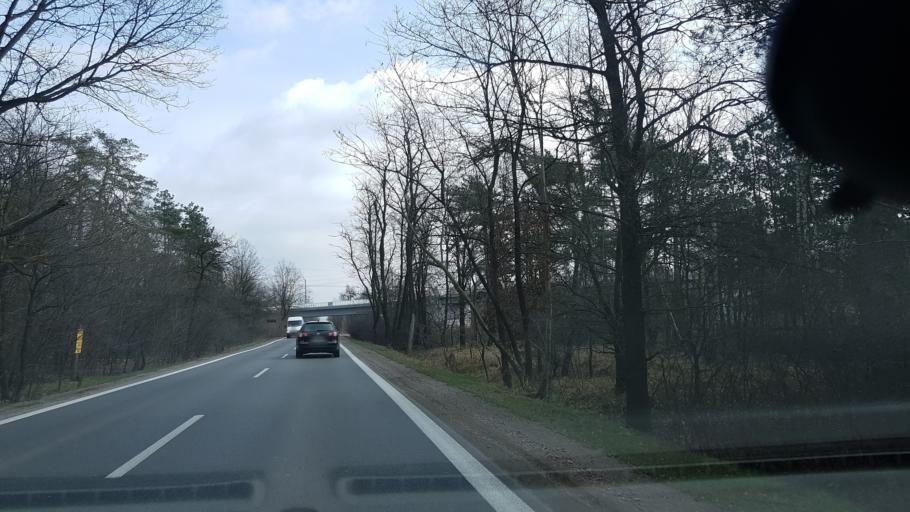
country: PL
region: Masovian Voivodeship
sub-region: Warszawa
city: Rembertow
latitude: 52.2562
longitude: 21.1888
